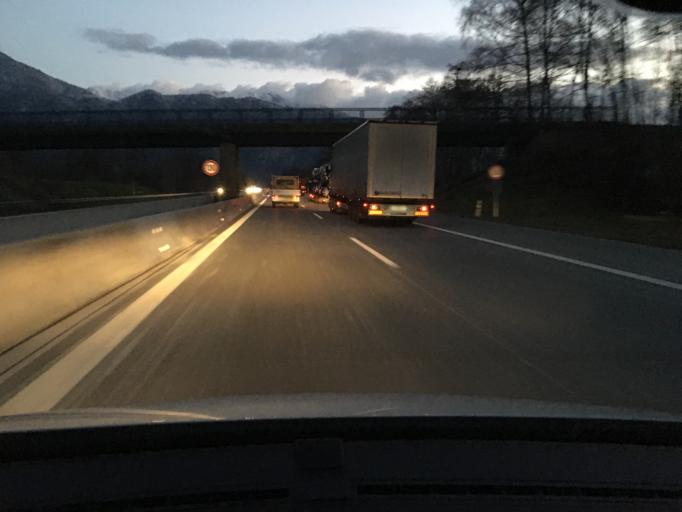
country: DE
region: Bavaria
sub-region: Upper Bavaria
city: Oberaudorf
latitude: 47.6423
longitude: 12.1919
